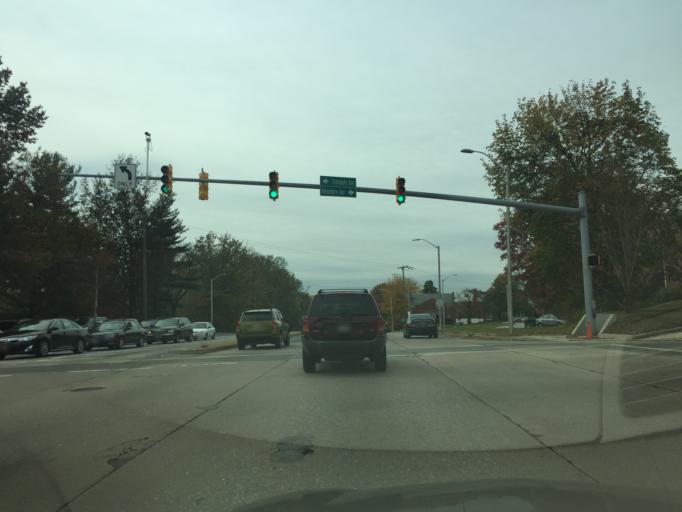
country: US
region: Maryland
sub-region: Baltimore County
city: Parkville
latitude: 39.3550
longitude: -76.5757
